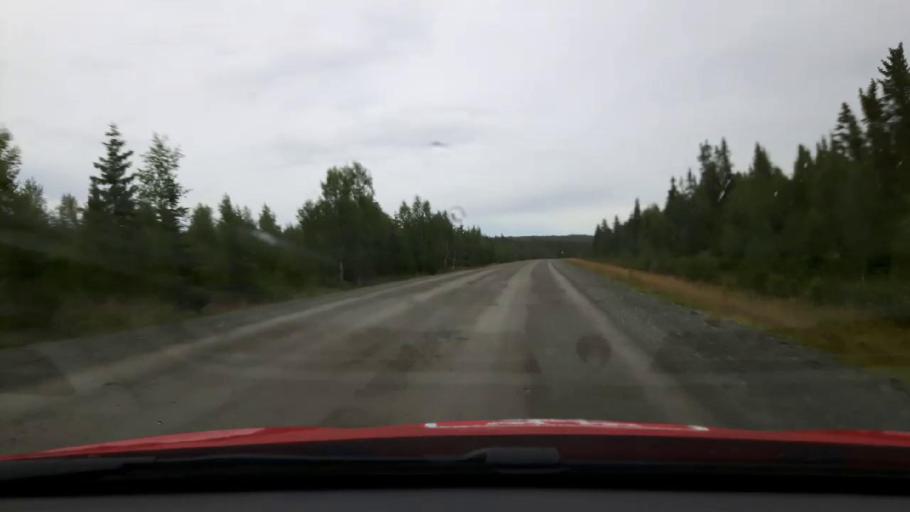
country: SE
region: Jaemtland
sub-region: Are Kommun
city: Are
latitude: 63.4687
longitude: 12.6065
